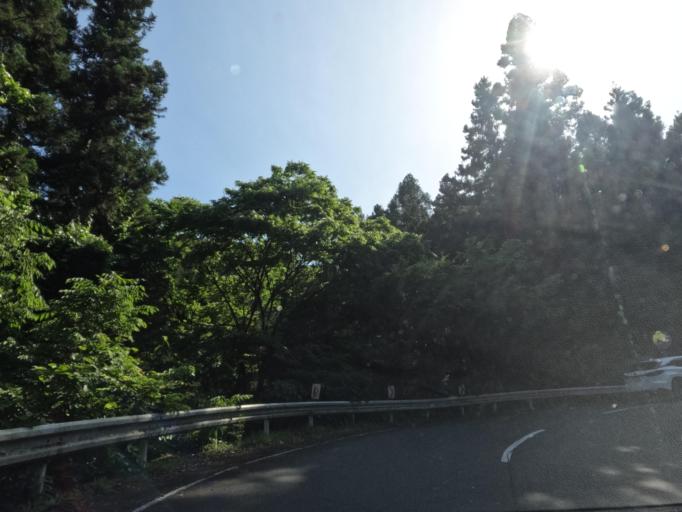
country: JP
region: Saitama
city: Yorii
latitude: 36.0457
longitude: 139.1703
